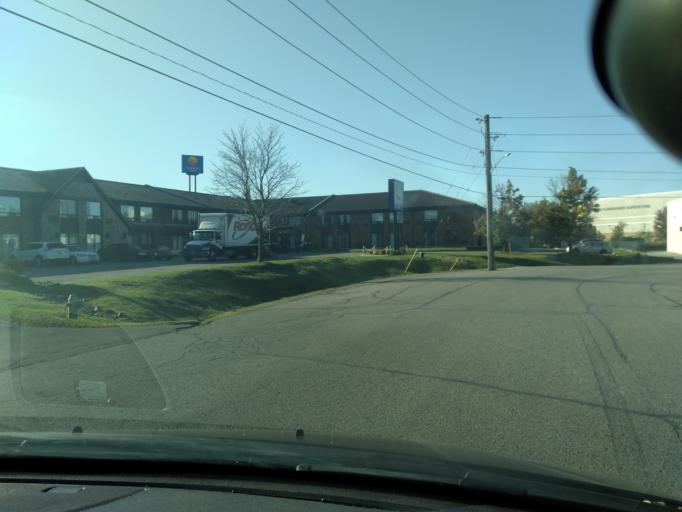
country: CA
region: Ontario
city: Newmarket
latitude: 44.0703
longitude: -79.4234
